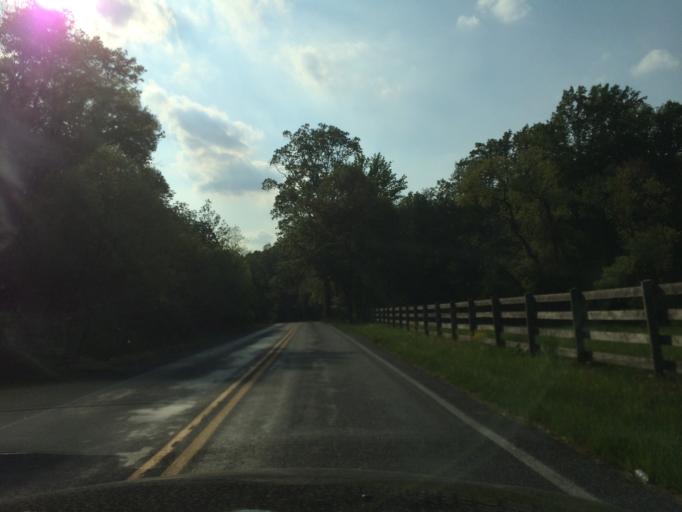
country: US
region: Maryland
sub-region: Carroll County
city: Sykesville
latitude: 39.2947
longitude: -77.0331
